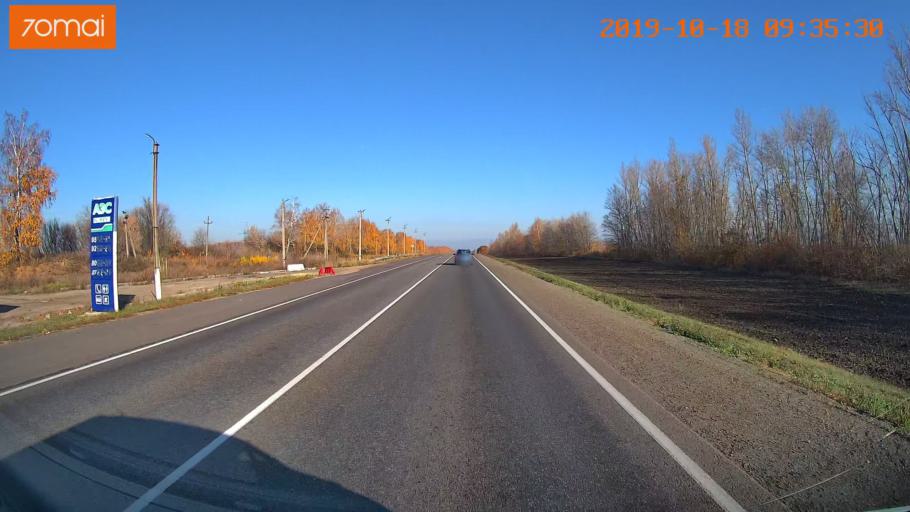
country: RU
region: Tula
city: Yefremov
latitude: 53.1931
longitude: 38.1484
